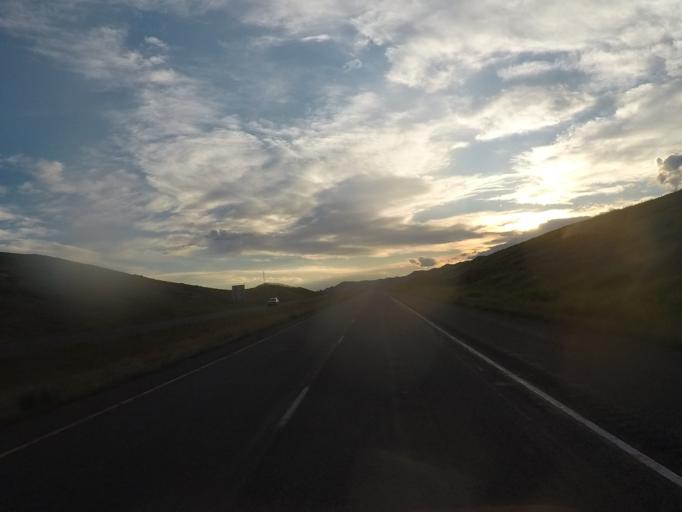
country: US
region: Montana
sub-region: Park County
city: Livingston
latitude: 45.6458
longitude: -110.5887
